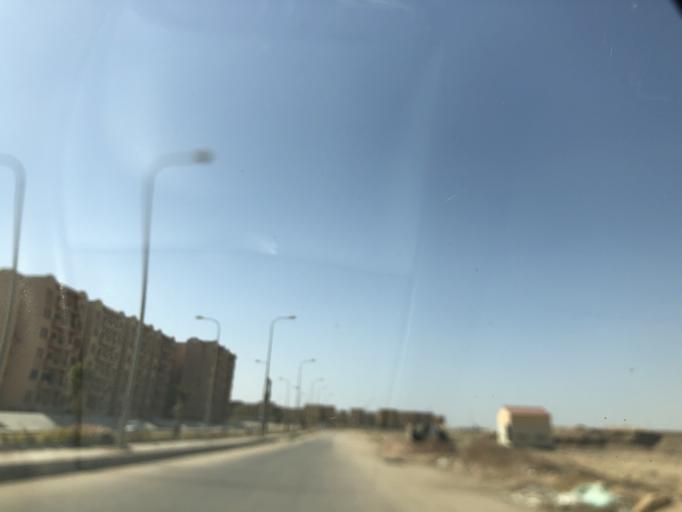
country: EG
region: Al Jizah
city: Madinat Sittah Uktubar
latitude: 29.9263
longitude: 31.0378
